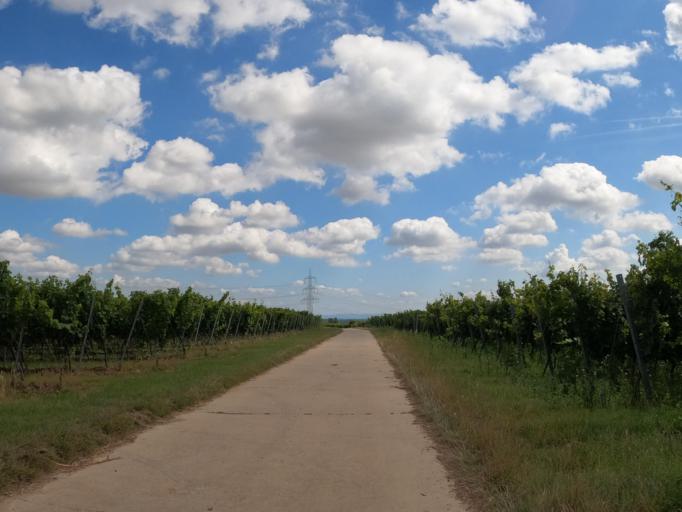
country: DE
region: Rheinland-Pfalz
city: Grosskarlbach
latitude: 49.5436
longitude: 8.2195
